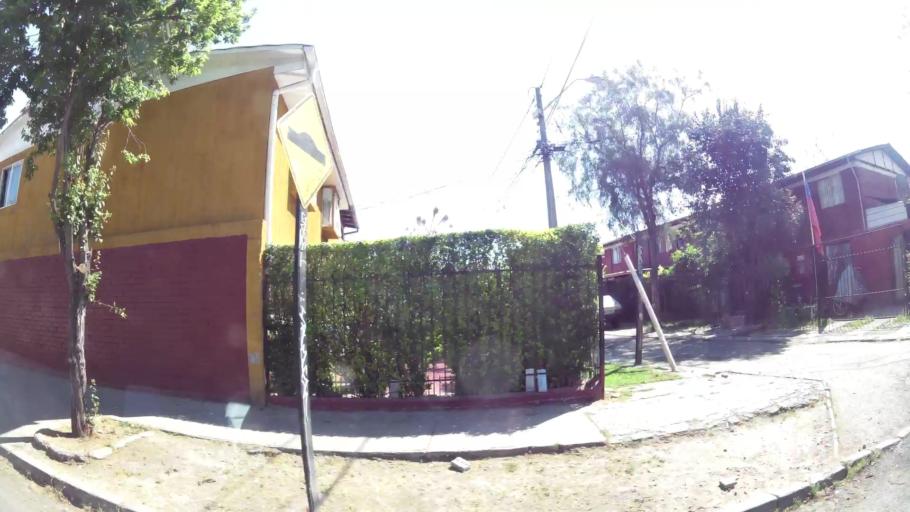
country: CL
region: Santiago Metropolitan
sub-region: Provincia de Santiago
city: Villa Presidente Frei, Nunoa, Santiago, Chile
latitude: -33.5303
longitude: -70.5635
